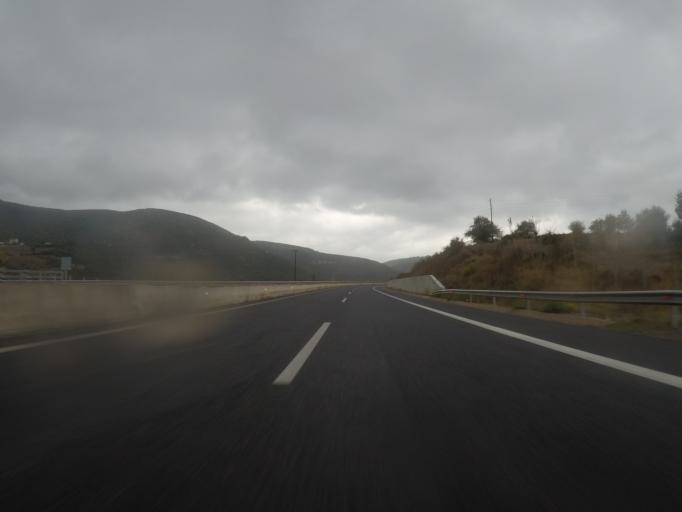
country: GR
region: Peloponnese
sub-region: Nomos Arkadias
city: Megalopoli
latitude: 37.3859
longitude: 22.2258
